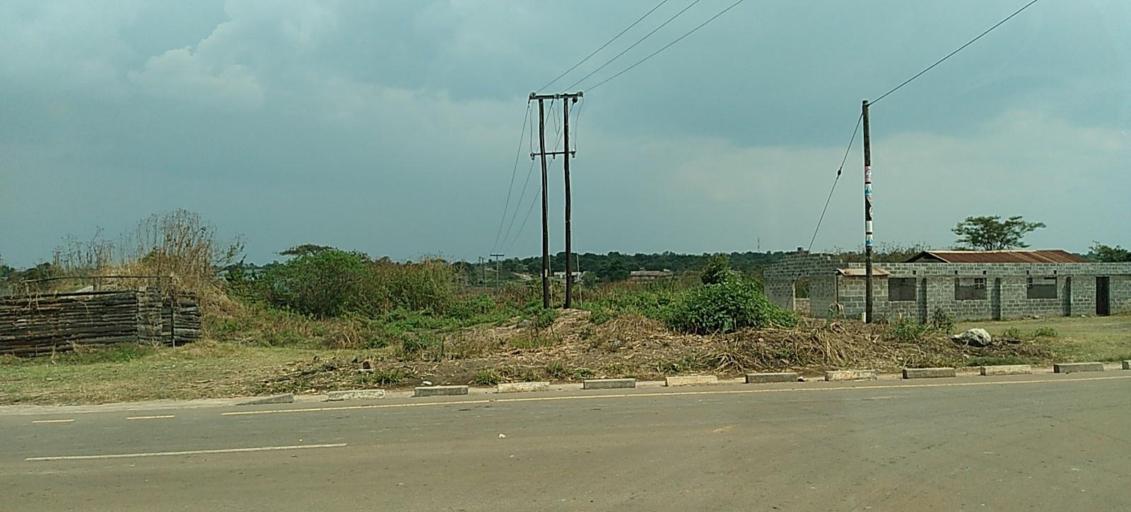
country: ZM
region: Copperbelt
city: Kalulushi
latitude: -12.8543
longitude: 28.1387
